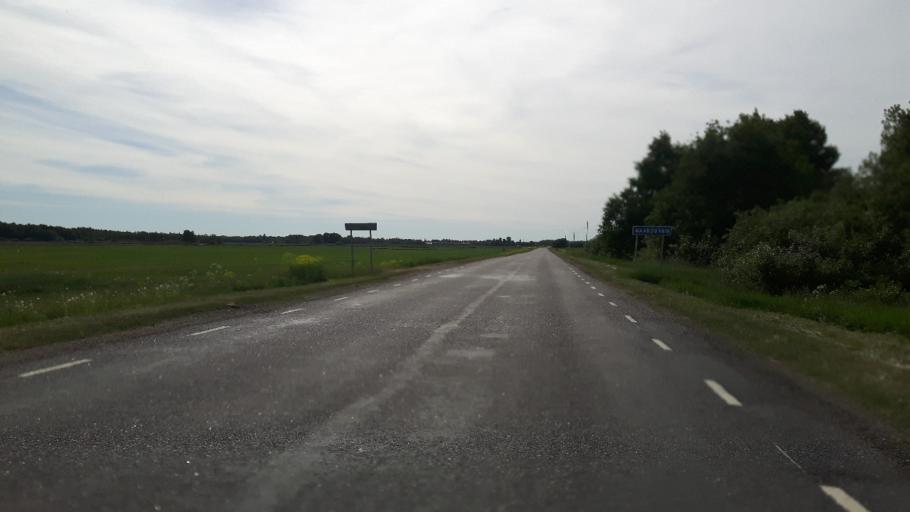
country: EE
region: Harju
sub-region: Maardu linn
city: Maardu
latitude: 59.4259
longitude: 25.0581
